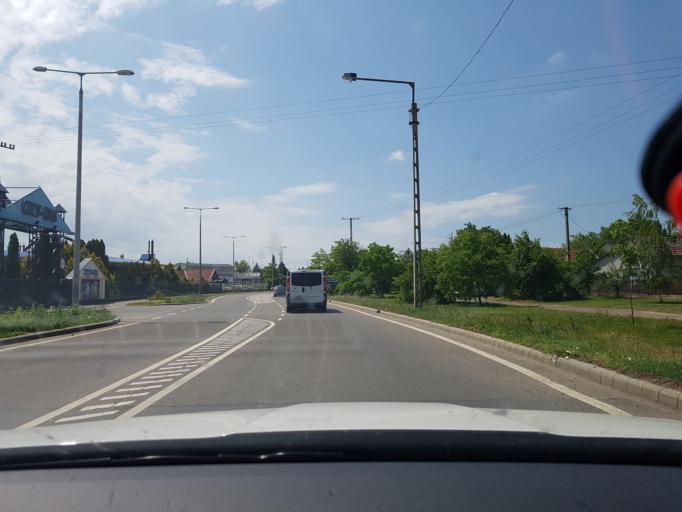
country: HU
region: Jasz-Nagykun-Szolnok
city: Tiszafured
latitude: 47.6076
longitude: 20.7608
